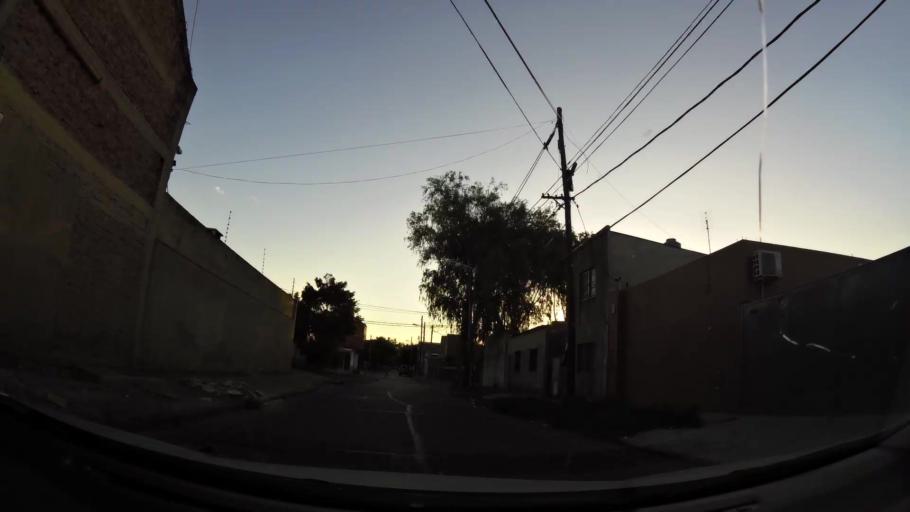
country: AR
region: Buenos Aires
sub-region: Partido de Tigre
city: Tigre
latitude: -34.4407
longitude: -58.5707
